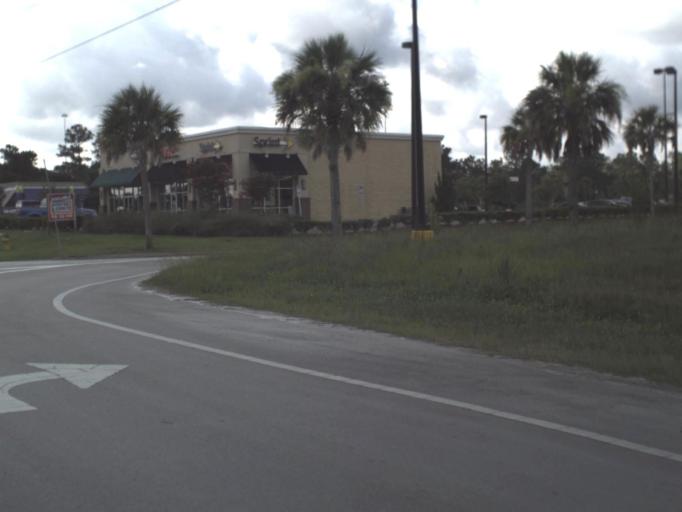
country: US
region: Florida
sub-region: Baker County
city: Macclenny
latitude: 30.2646
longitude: -82.1075
